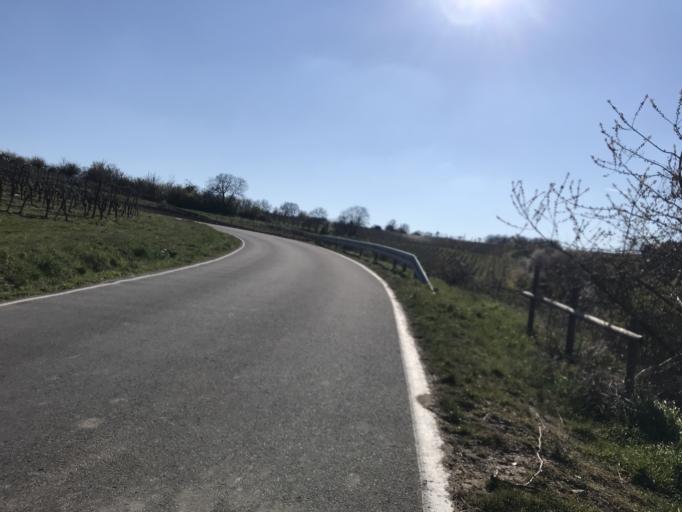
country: DE
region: Rheinland-Pfalz
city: Ingelheim am Rhein
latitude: 49.9568
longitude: 8.0427
